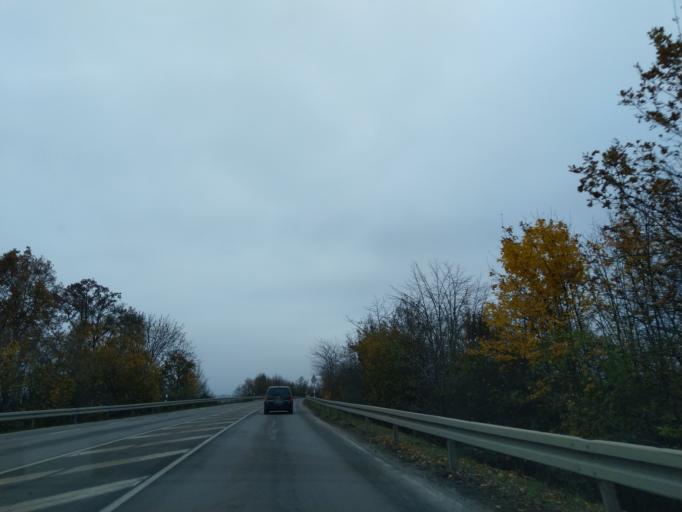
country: DE
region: Bavaria
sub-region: Lower Bavaria
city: Stephansposching
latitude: 48.7945
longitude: 12.8301
